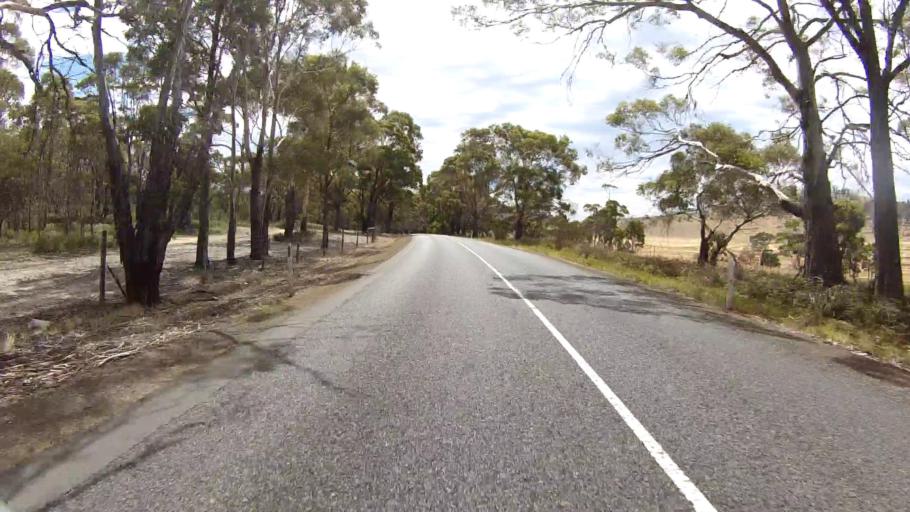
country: AU
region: Tasmania
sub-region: Sorell
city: Sorell
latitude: -42.8806
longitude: 147.6750
